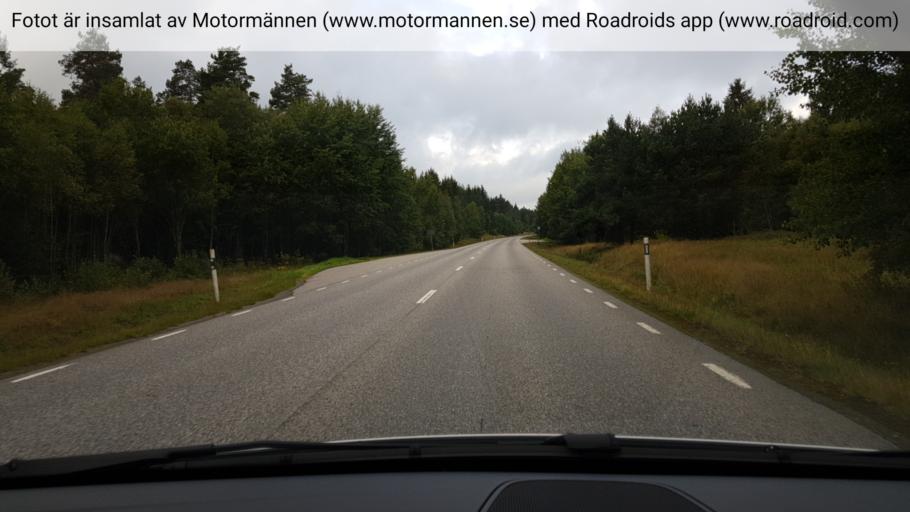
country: SE
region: Vaestra Goetaland
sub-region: Herrljunga Kommun
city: Herrljunga
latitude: 58.0608
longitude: 13.0704
